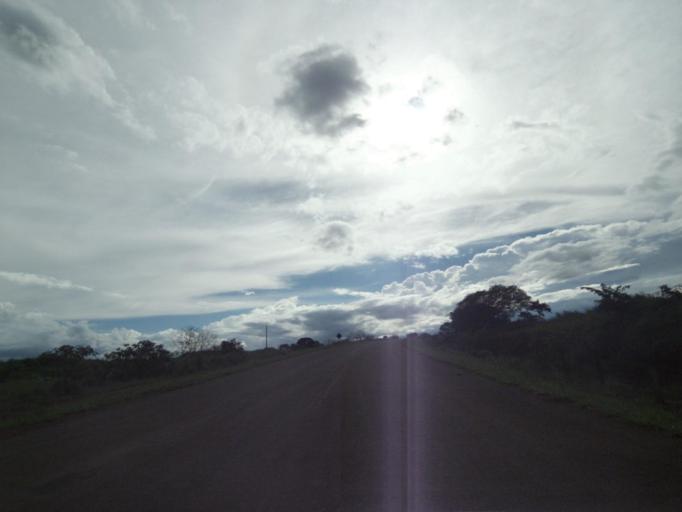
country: BR
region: Goias
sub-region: Jaragua
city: Jaragua
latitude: -15.8818
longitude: -49.4338
